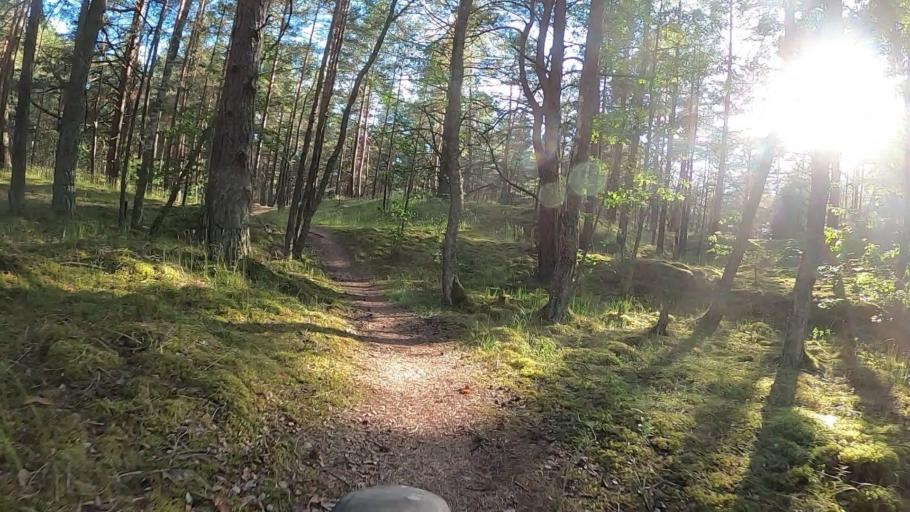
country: LV
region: Carnikava
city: Carnikava
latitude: 57.1337
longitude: 24.2313
